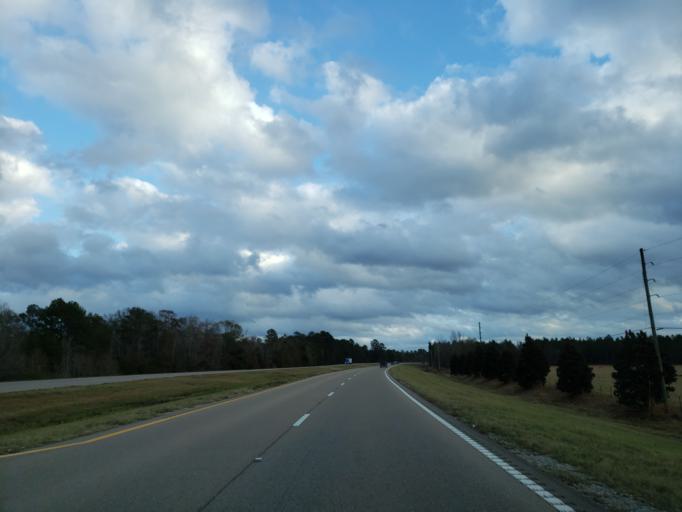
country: US
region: Mississippi
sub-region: Perry County
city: New Augusta
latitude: 31.1410
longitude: -88.8641
